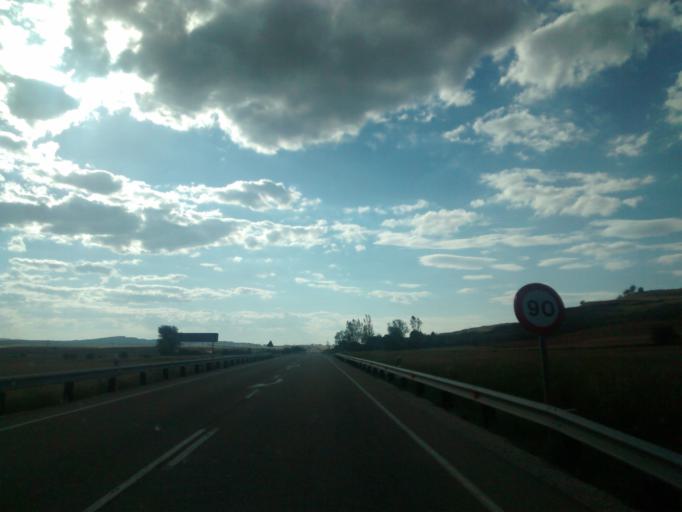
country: ES
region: Castille and Leon
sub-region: Provincia de Burgos
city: Basconcillos del Tozo
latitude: 42.6574
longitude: -3.9049
